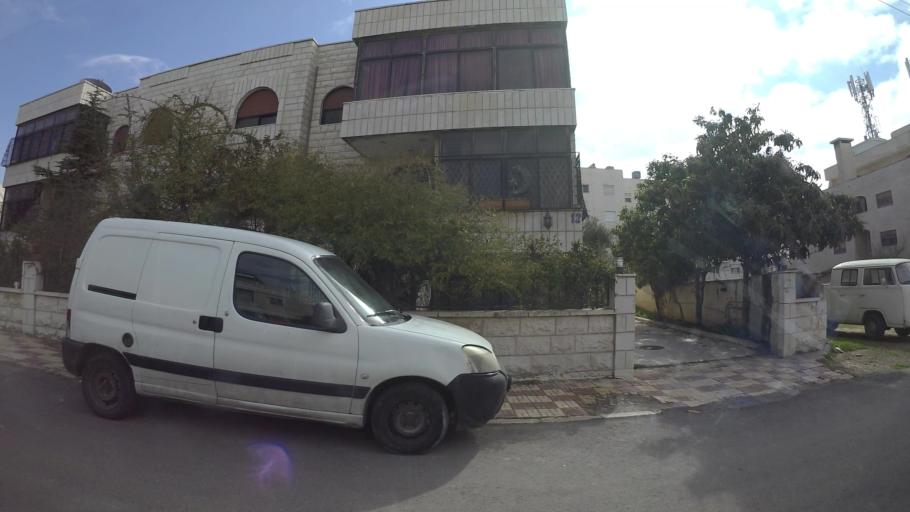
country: JO
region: Amman
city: Wadi as Sir
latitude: 31.9514
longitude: 35.8454
